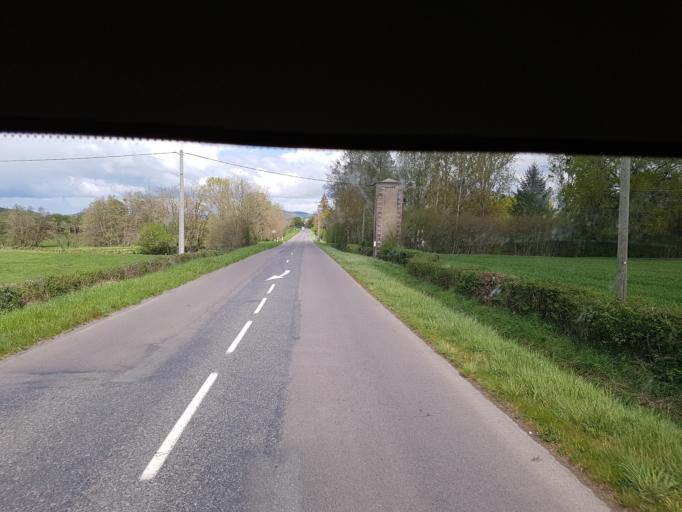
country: FR
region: Bourgogne
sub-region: Departement de Saone-et-Loire
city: Etang-sur-Arroux
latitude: 46.8263
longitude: 4.1767
